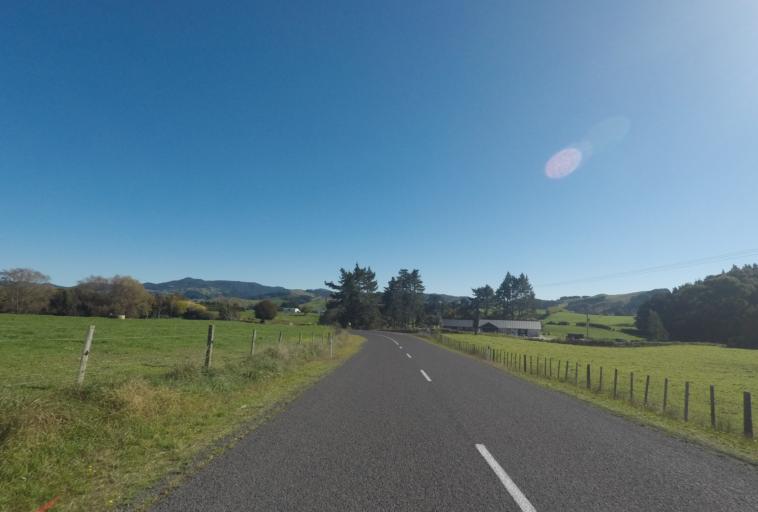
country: NZ
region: Bay of Plenty
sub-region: Western Bay of Plenty District
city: Waihi Beach
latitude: -37.3852
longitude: 175.8941
